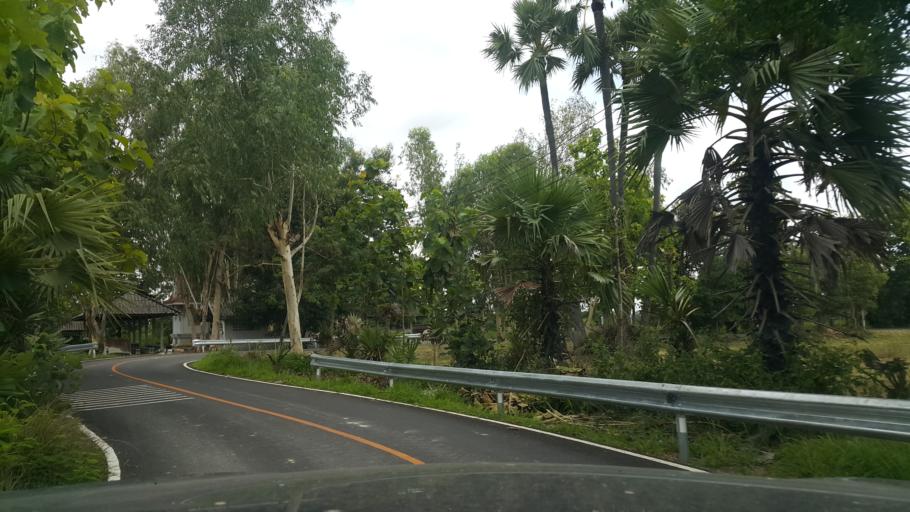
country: TH
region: Lamphun
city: Ban Thi
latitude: 18.6577
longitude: 99.1522
